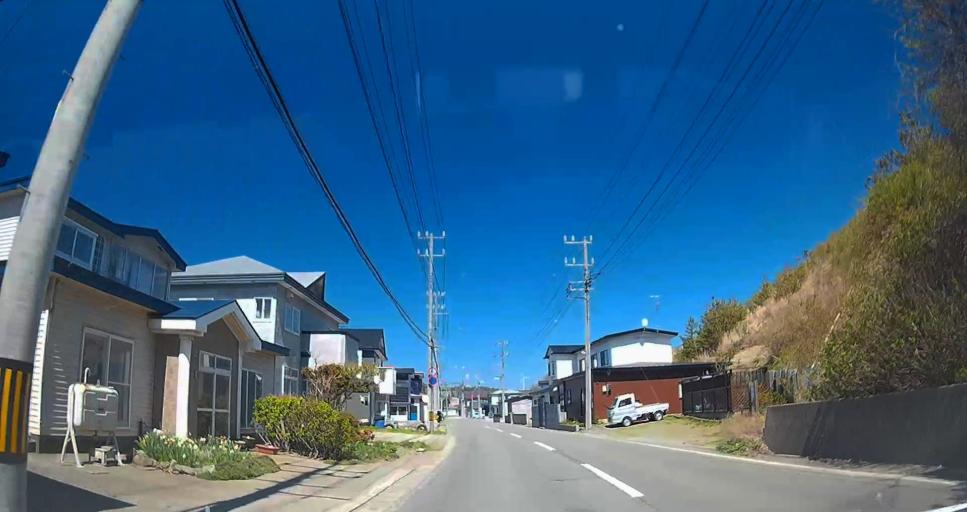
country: JP
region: Hokkaido
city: Hakodate
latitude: 41.5017
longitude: 140.9097
